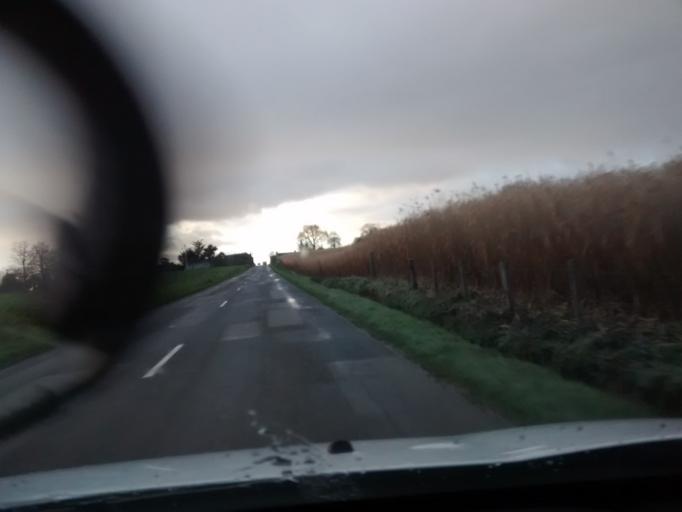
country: FR
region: Brittany
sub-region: Departement d'Ille-et-Vilaine
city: Bais
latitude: 47.9940
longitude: -1.2869
